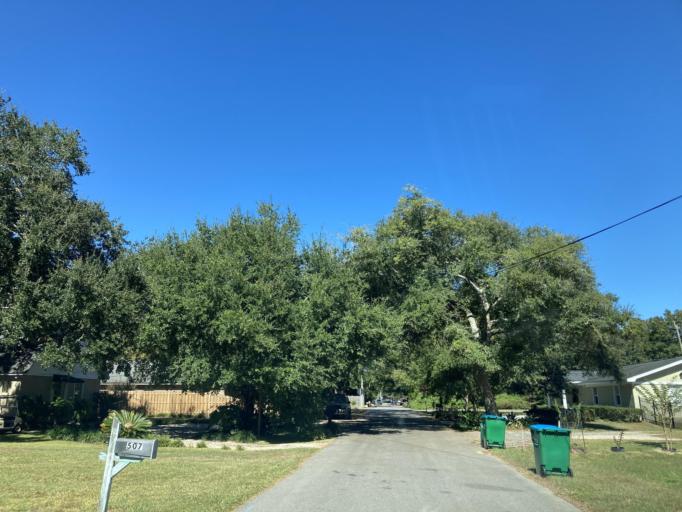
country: US
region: Mississippi
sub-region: Jackson County
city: Ocean Springs
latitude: 30.4107
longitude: -88.8246
